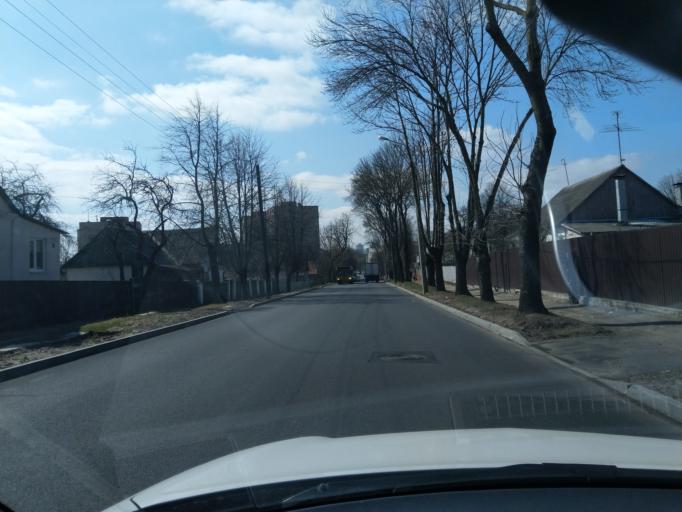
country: BY
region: Minsk
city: Syenitsa
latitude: 53.8697
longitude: 27.5126
